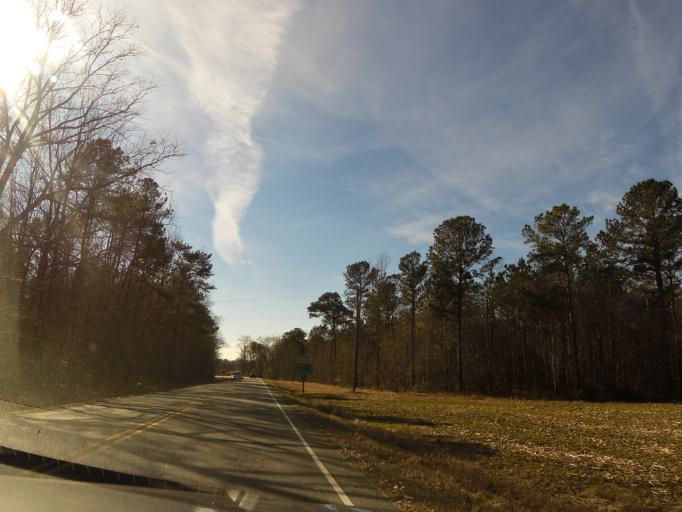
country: US
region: Virginia
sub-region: Isle of Wight County
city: Isle of Wight
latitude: 36.8718
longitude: -76.7333
